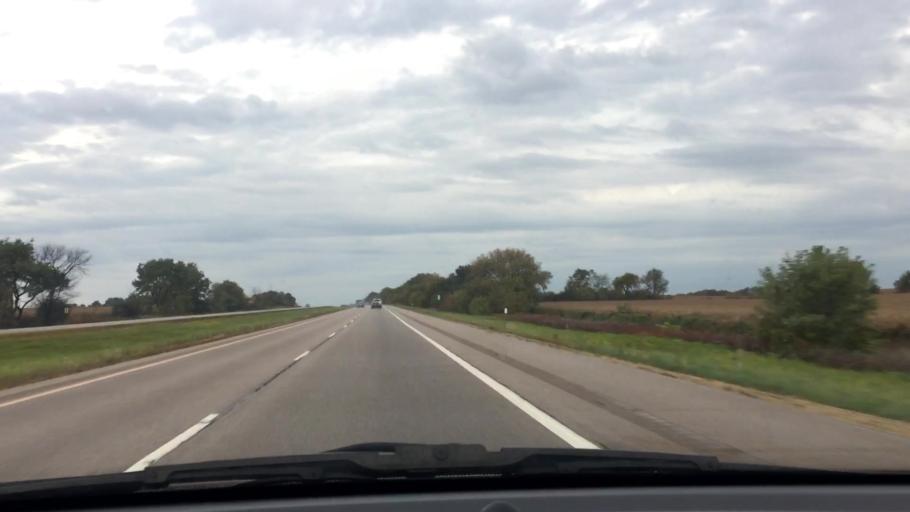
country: US
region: Wisconsin
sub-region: Rock County
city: Clinton
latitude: 42.5728
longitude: -88.8436
